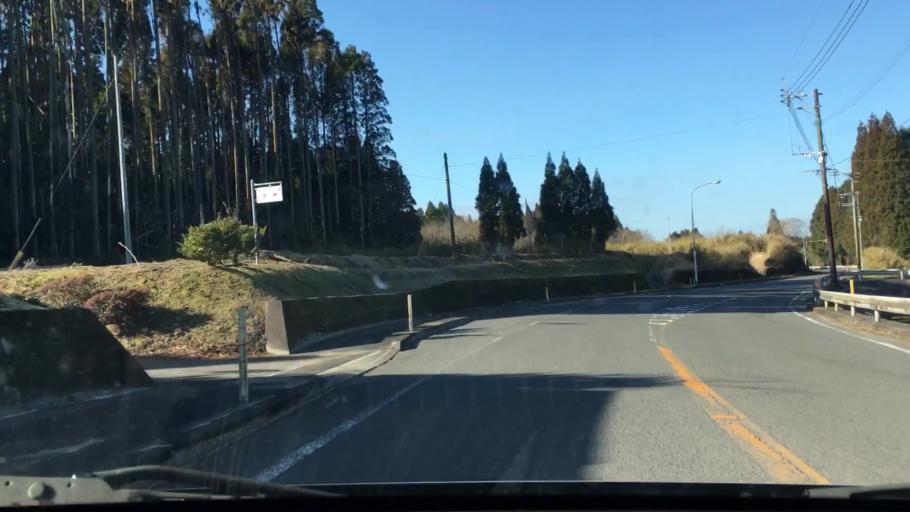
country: JP
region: Kagoshima
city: Sueyoshicho-ninokata
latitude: 31.6784
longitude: 130.9343
